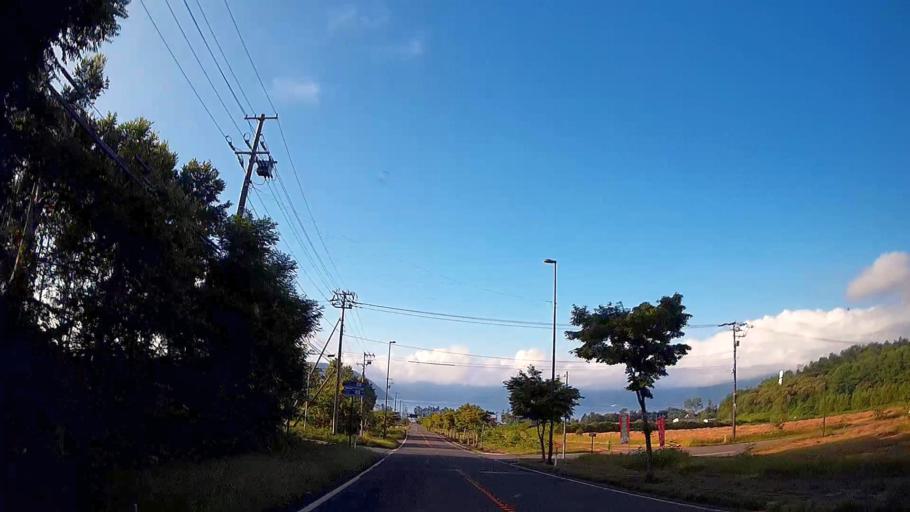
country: JP
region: Hokkaido
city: Date
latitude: 42.5524
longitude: 140.8621
